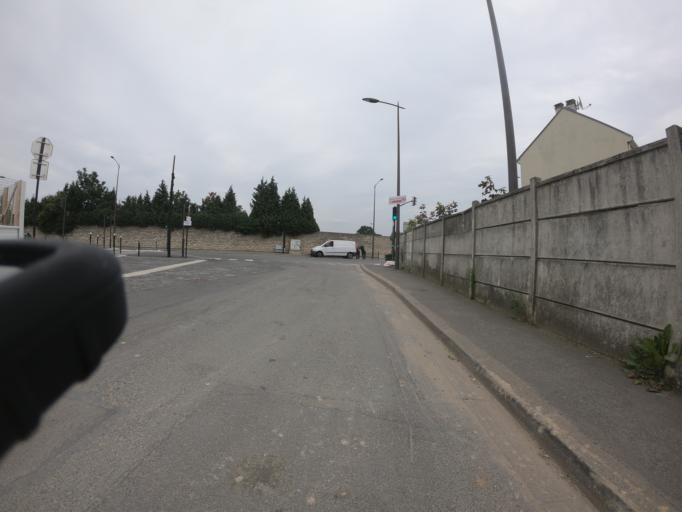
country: FR
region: Ile-de-France
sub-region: Departement du Val-de-Marne
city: Thiais
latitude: 48.7664
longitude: 2.3835
